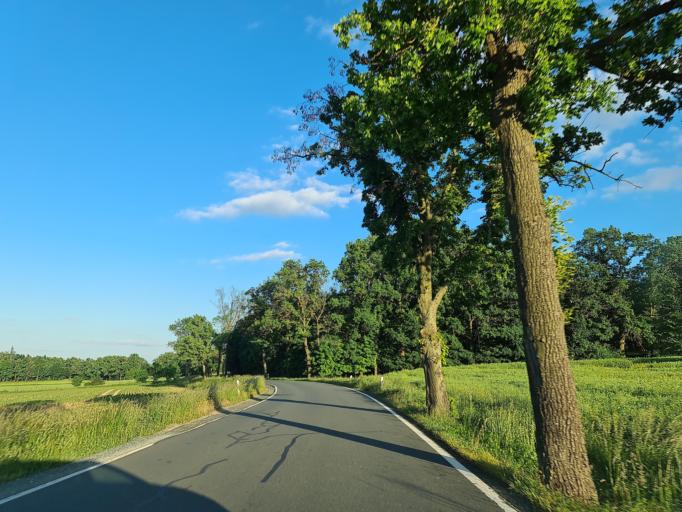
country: DE
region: Saxony
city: Weischlitz
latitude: 50.4545
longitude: 12.0353
